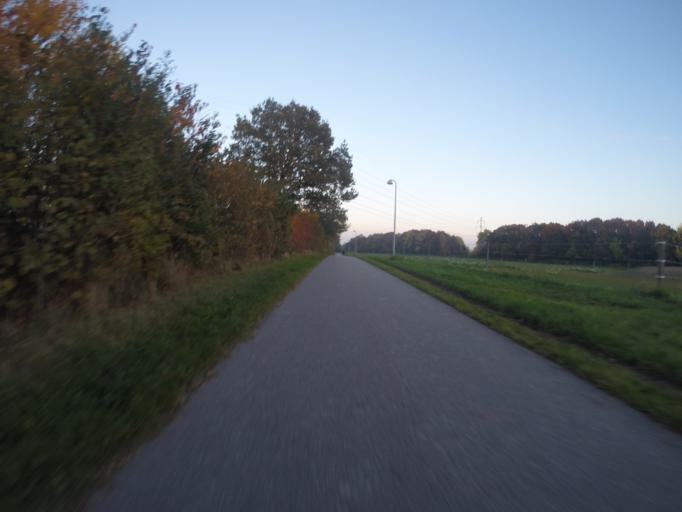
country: DK
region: Capital Region
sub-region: Hoje-Taastrup Kommune
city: Taastrup
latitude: 55.6672
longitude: 12.3044
